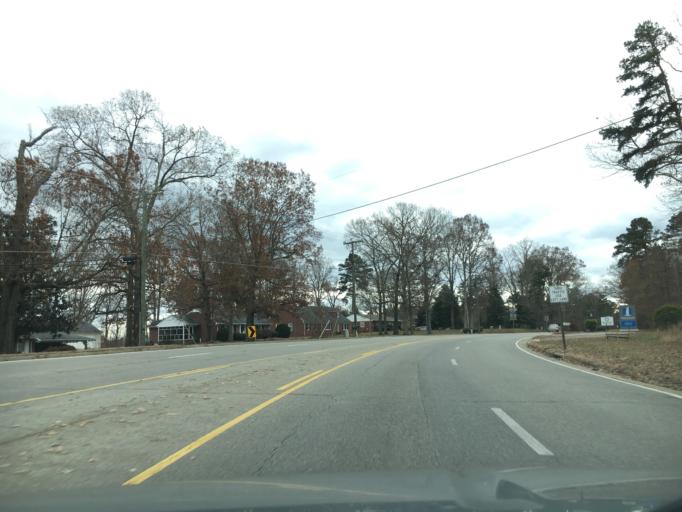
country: US
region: Virginia
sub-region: Halifax County
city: South Boston
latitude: 36.7320
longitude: -78.9058
